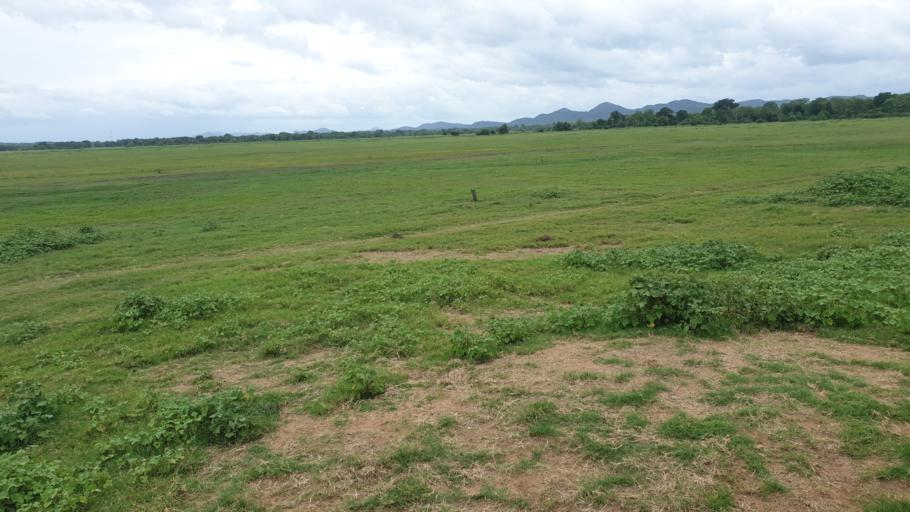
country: LK
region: North Central
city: Polonnaruwa
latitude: 8.1296
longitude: 80.9070
